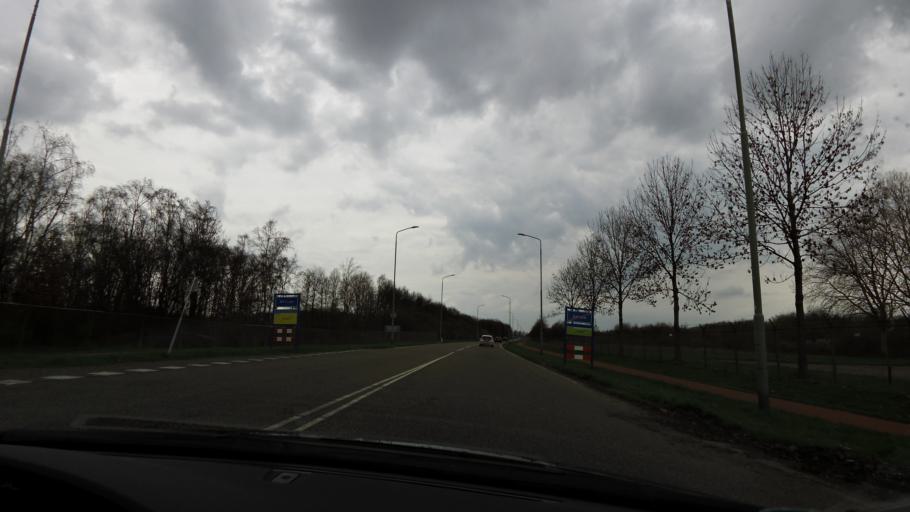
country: NL
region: Limburg
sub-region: Gemeente Stein
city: Urmond
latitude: 50.9848
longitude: 5.8048
